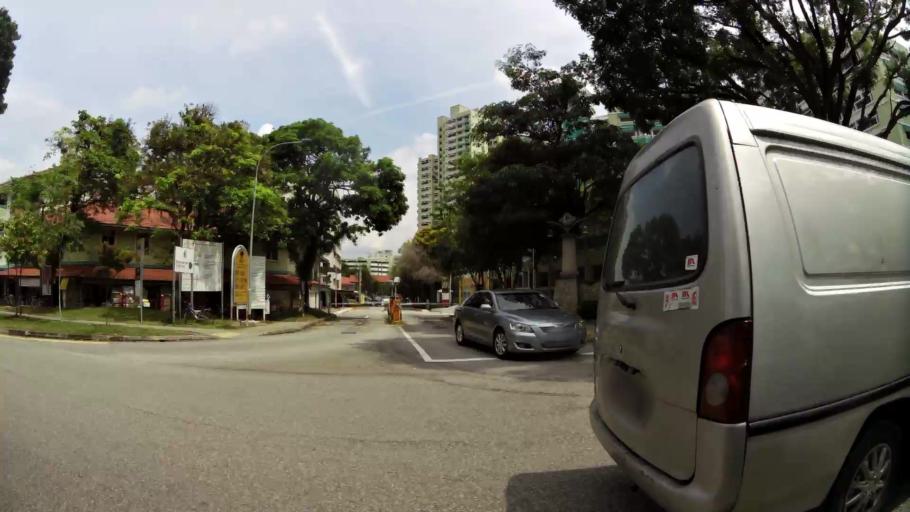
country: SG
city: Singapore
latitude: 1.3463
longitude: 103.7572
